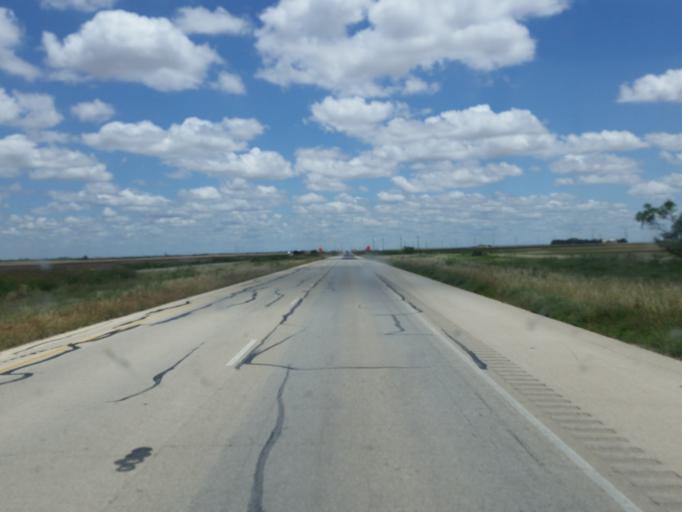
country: US
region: Texas
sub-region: Nolan County
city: Roscoe
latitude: 32.4855
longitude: -100.6259
